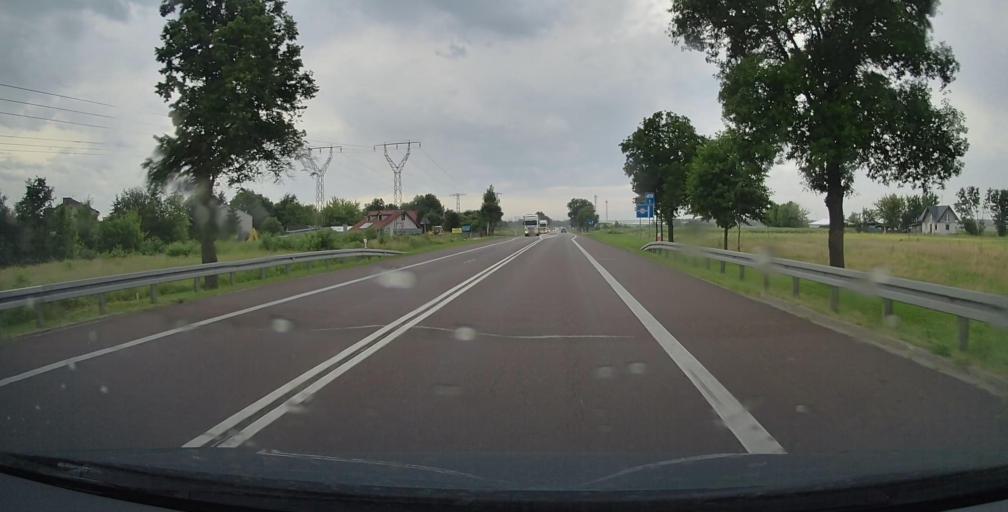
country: PL
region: Lublin Voivodeship
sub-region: Powiat bialski
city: Miedzyrzec Podlaski
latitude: 52.0002
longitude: 22.7808
